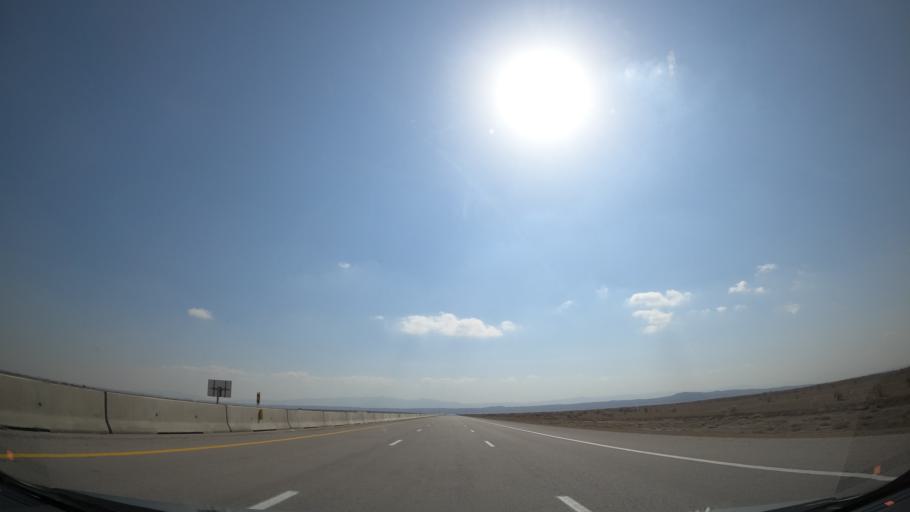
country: IR
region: Alborz
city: Nazarabad
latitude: 35.8556
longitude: 50.4801
